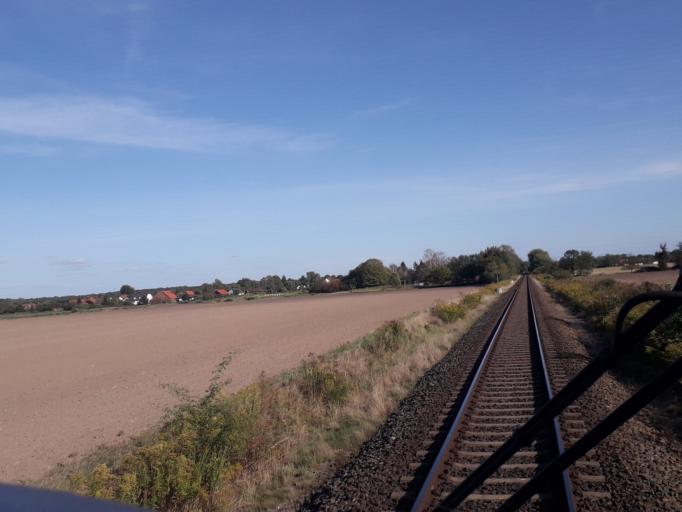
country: DE
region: Brandenburg
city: Kremmen
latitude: 52.7427
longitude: 13.0662
